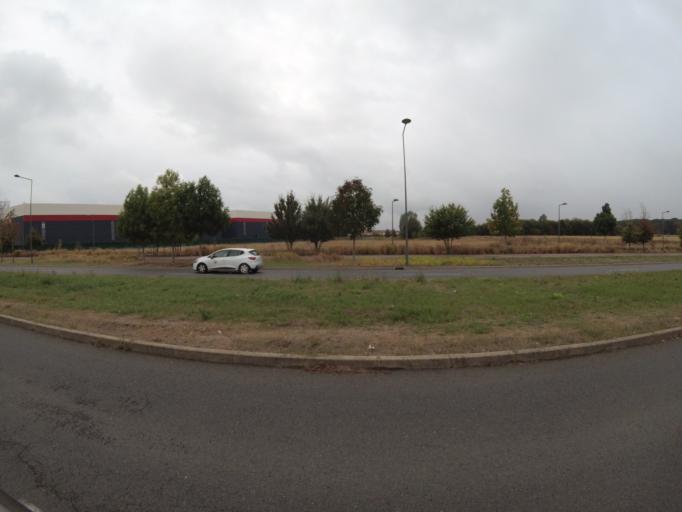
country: FR
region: Ile-de-France
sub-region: Departement de Seine-et-Marne
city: Chanteloup-en-Brie
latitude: 48.8624
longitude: 2.7448
